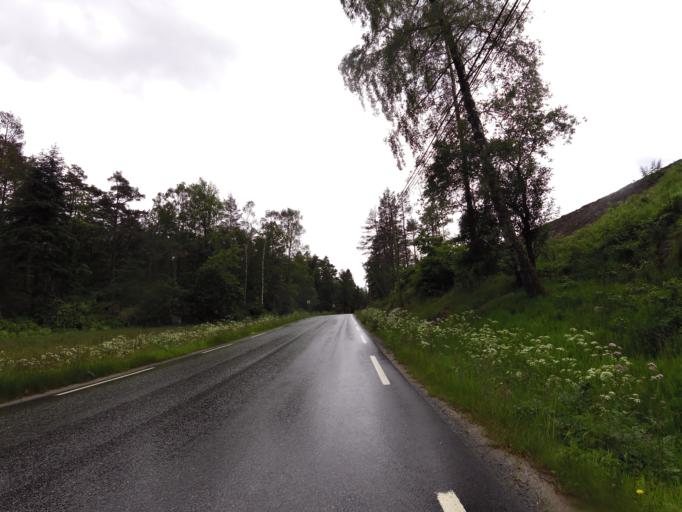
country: NO
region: Vest-Agder
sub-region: Mandal
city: Mandal
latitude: 58.0210
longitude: 7.5161
